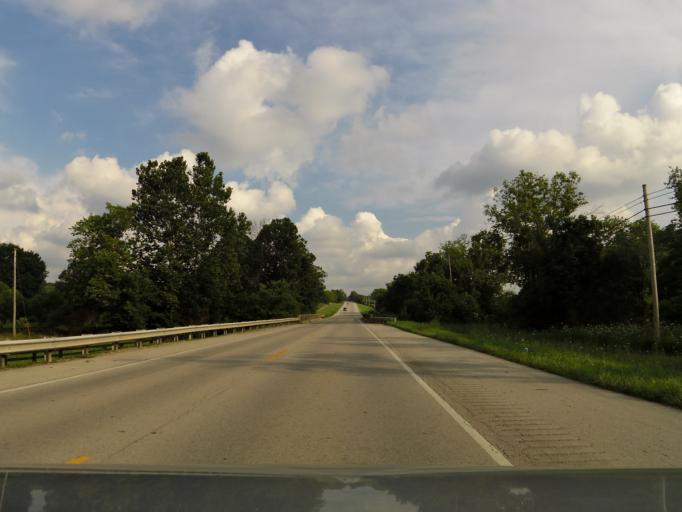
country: US
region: Kentucky
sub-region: Bourbon County
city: Paris
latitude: 38.2645
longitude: -84.2955
